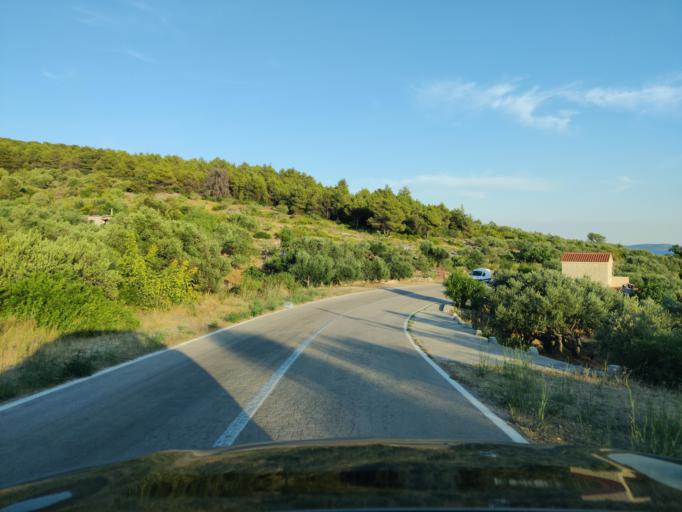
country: HR
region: Sibensko-Kniniska
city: Tribunj
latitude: 43.7856
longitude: 15.7267
